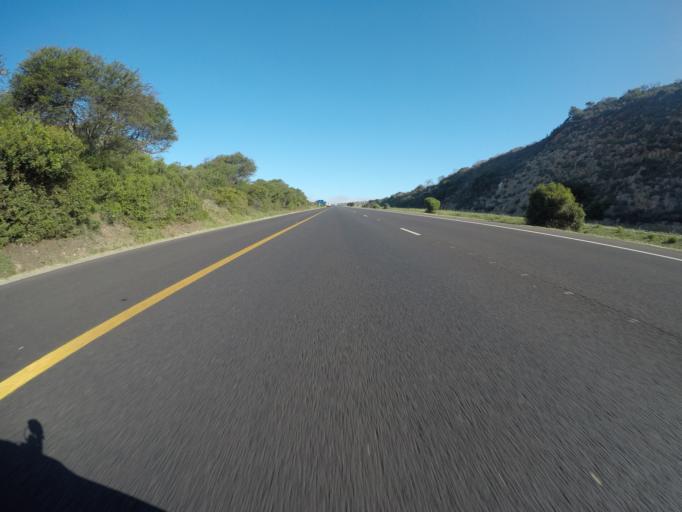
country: ZA
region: Western Cape
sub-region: Eden District Municipality
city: Mossel Bay
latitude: -34.1544
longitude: 22.0994
